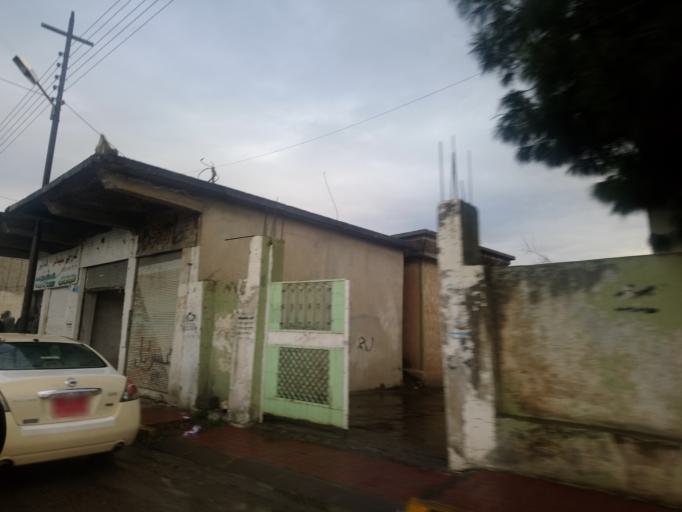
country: IQ
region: As Sulaymaniyah
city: Qeladize
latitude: 36.1851
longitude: 45.1177
